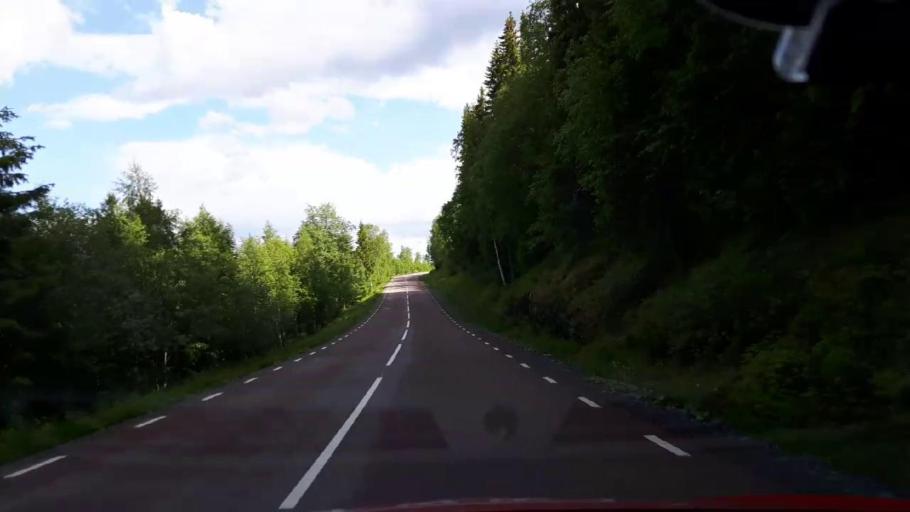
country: SE
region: Jaemtland
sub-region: Krokoms Kommun
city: Valla
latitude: 63.9512
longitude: 14.2134
